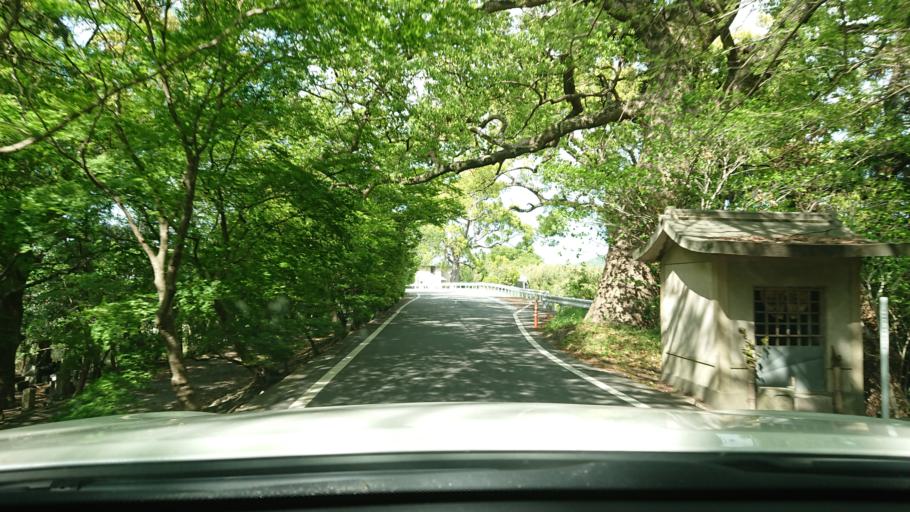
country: JP
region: Tokushima
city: Komatsushimacho
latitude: 34.0053
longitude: 134.5518
